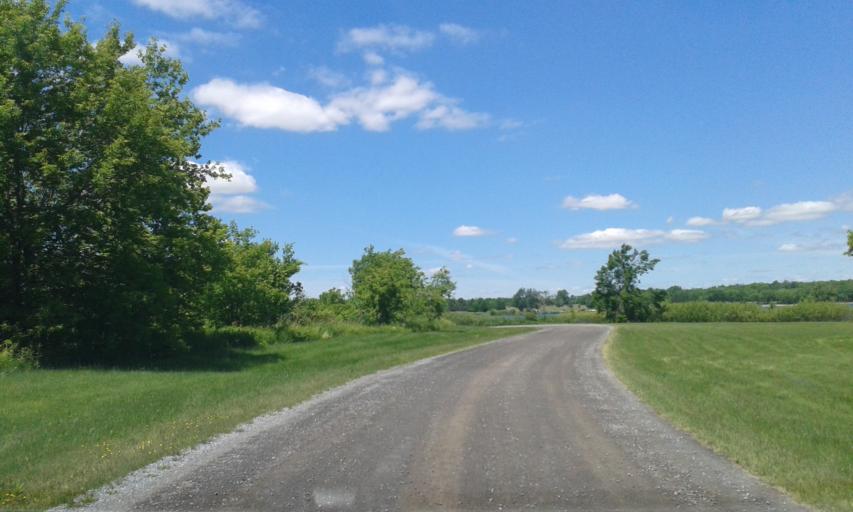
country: US
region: New York
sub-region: St. Lawrence County
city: Massena
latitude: 45.0044
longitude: -74.8891
